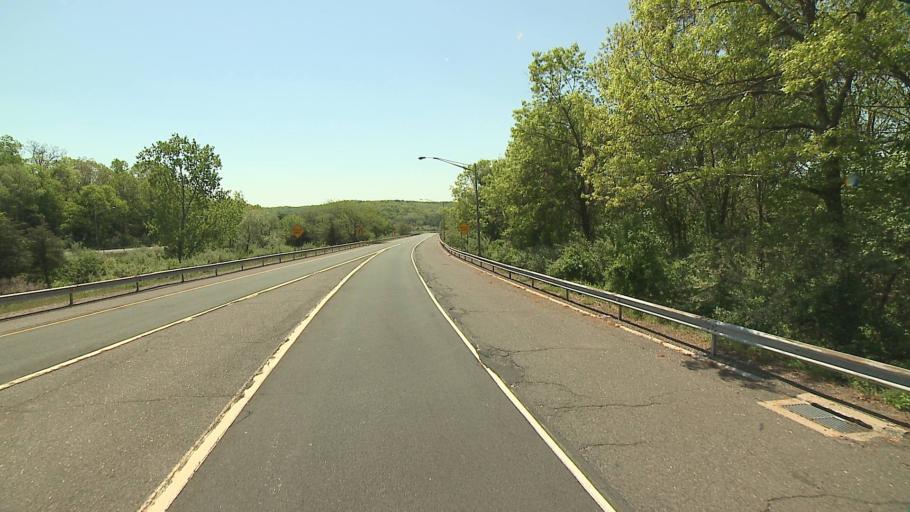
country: US
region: Connecticut
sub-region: Fairfield County
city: Newtown
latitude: 41.4113
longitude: -73.2680
